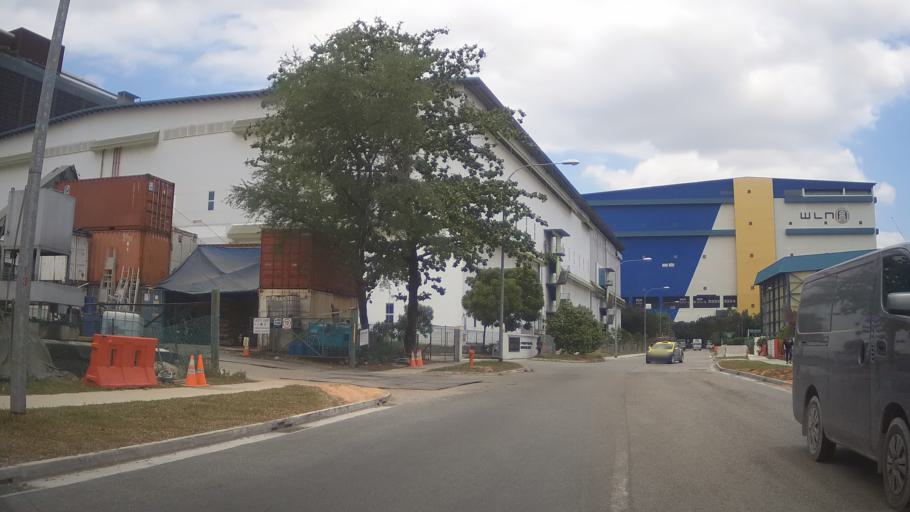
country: SG
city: Singapore
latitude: 1.3112
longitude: 103.7228
